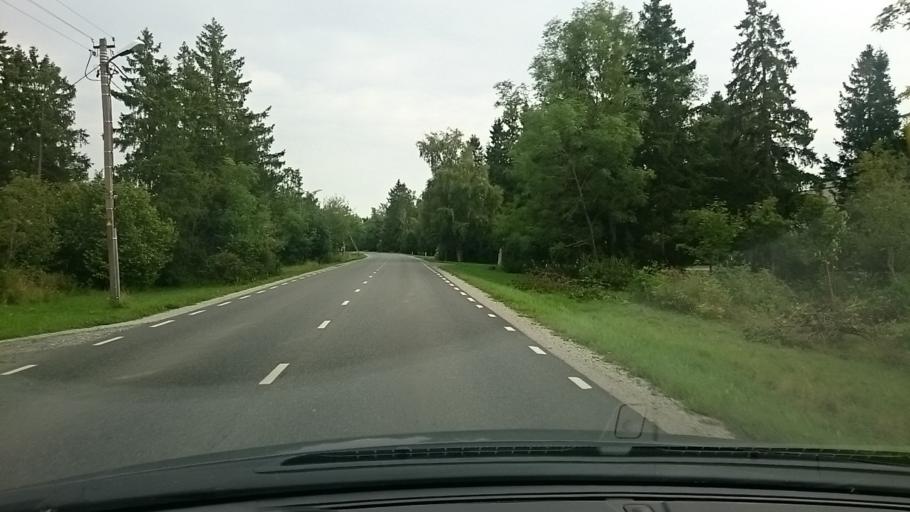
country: EE
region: Harju
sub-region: Harku vald
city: Tabasalu
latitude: 59.4273
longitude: 24.5266
